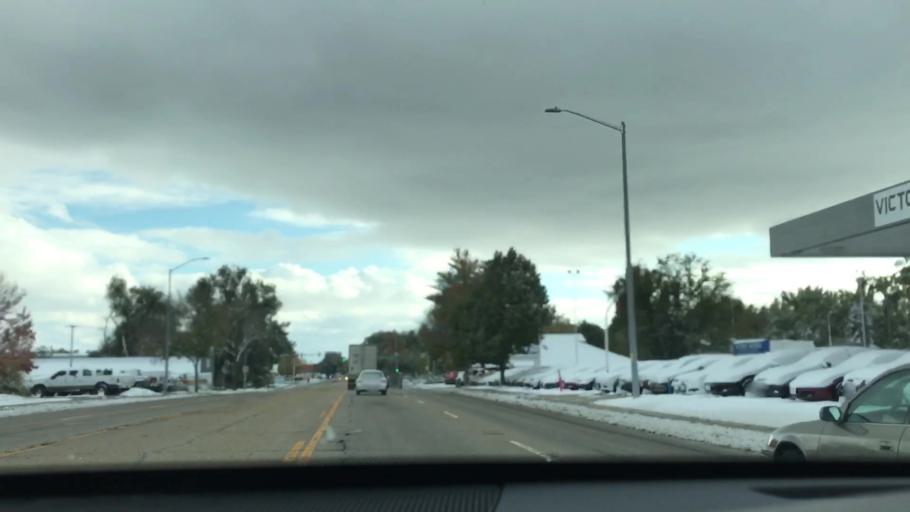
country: US
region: Colorado
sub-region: Boulder County
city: Longmont
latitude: 40.1829
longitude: -105.1024
